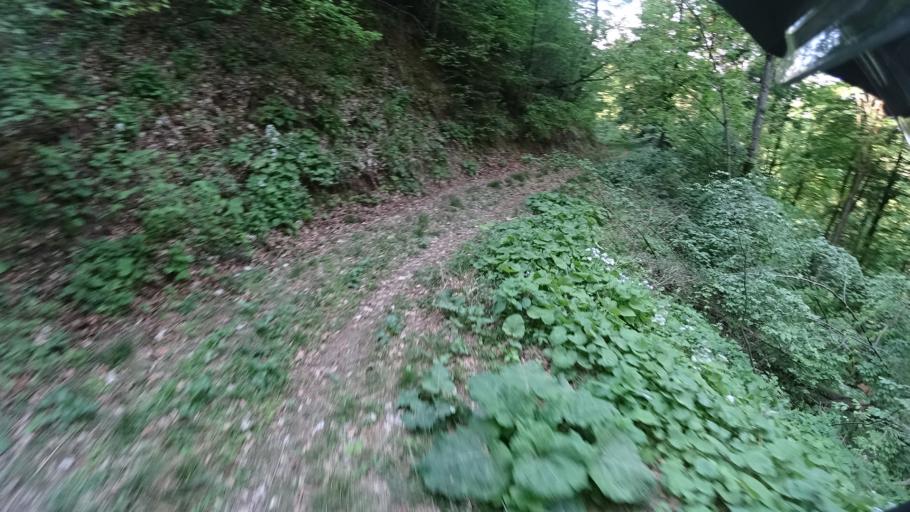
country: HR
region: Grad Zagreb
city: Kasina
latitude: 45.9455
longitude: 15.9783
